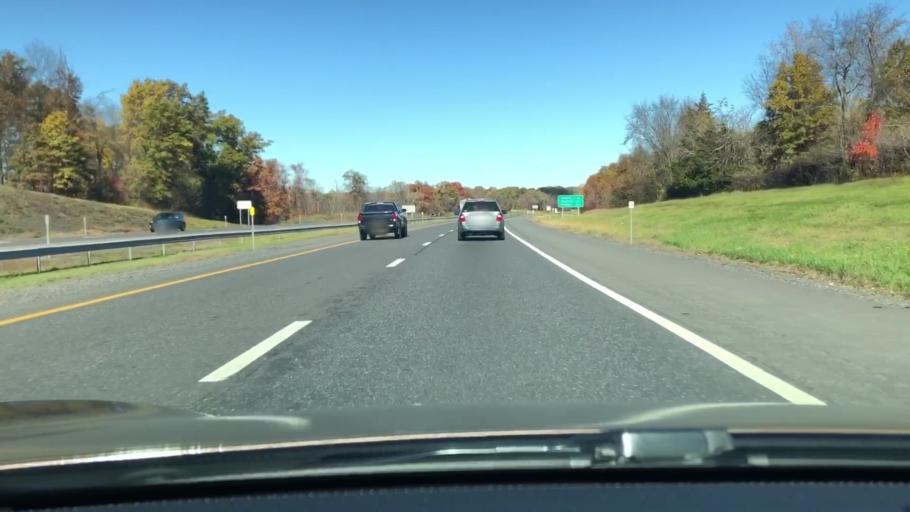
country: US
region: New York
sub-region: Ulster County
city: New Paltz
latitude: 41.7431
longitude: -74.0644
